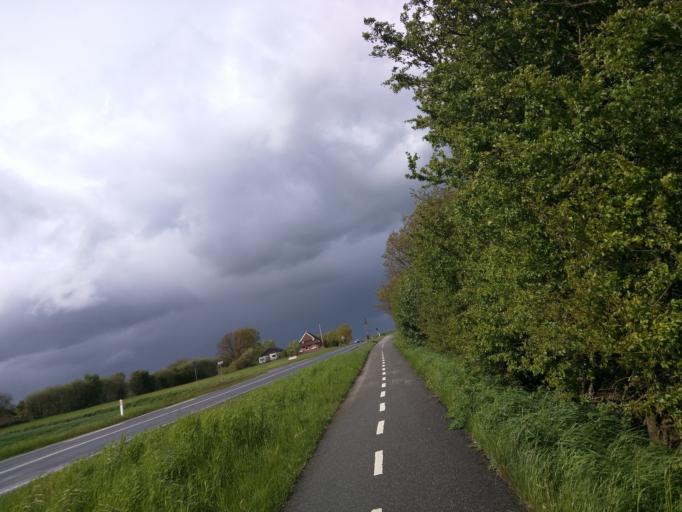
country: DK
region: Central Jutland
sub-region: Silkeborg Kommune
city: Kjellerup
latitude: 56.3039
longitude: 9.4247
